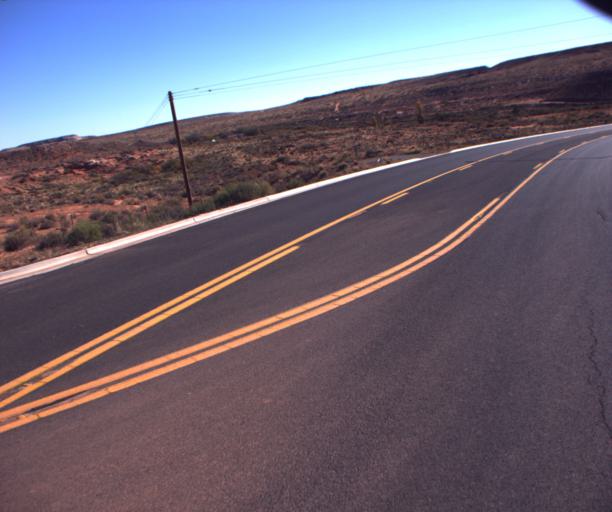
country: US
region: Arizona
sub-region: Coconino County
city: Tuba City
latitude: 36.1137
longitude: -111.2217
